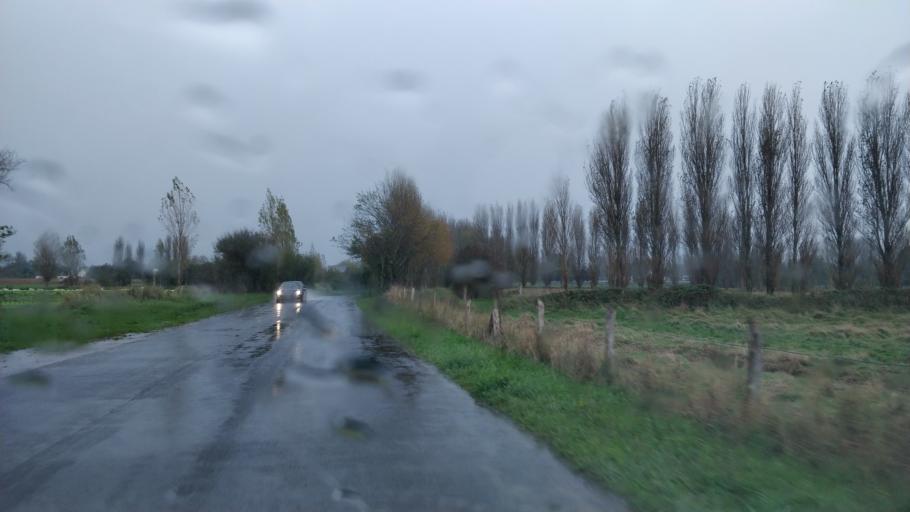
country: FR
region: Lower Normandy
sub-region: Departement de la Manche
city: Brehal
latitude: 48.9021
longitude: -1.5499
